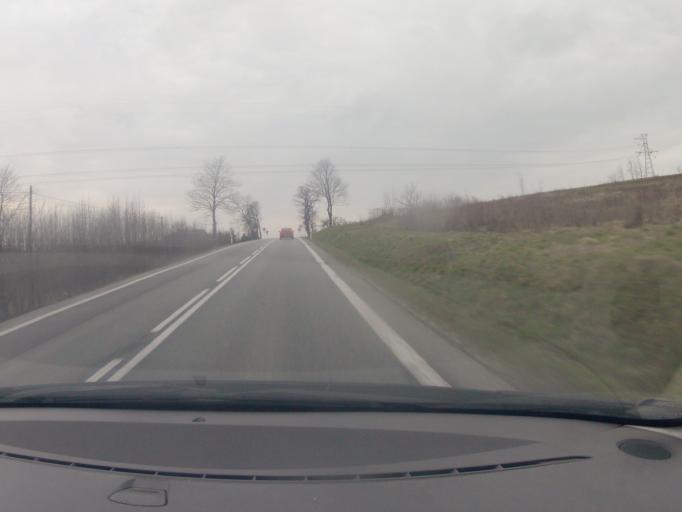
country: PL
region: Subcarpathian Voivodeship
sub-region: Powiat debicki
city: Slotowa
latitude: 49.9184
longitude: 21.3433
